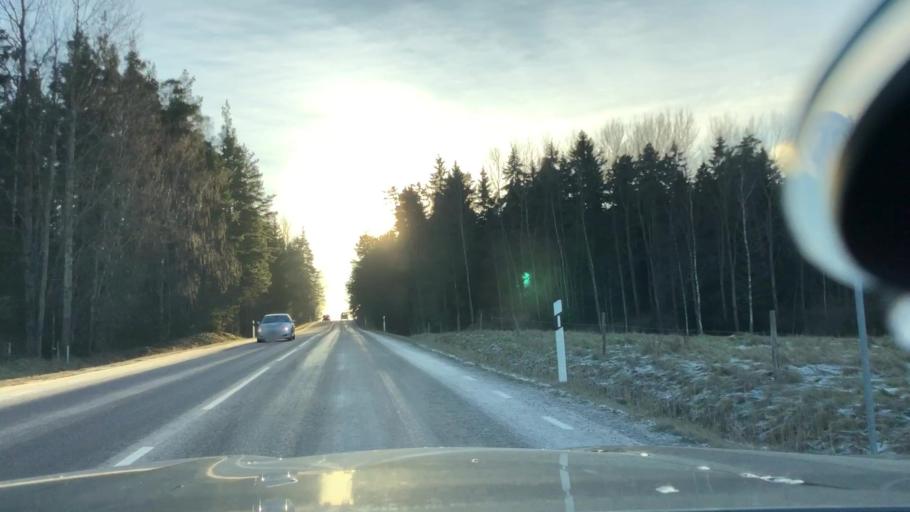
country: SE
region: Stockholm
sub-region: Sodertalje Kommun
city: Pershagen
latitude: 59.0445
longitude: 17.6050
